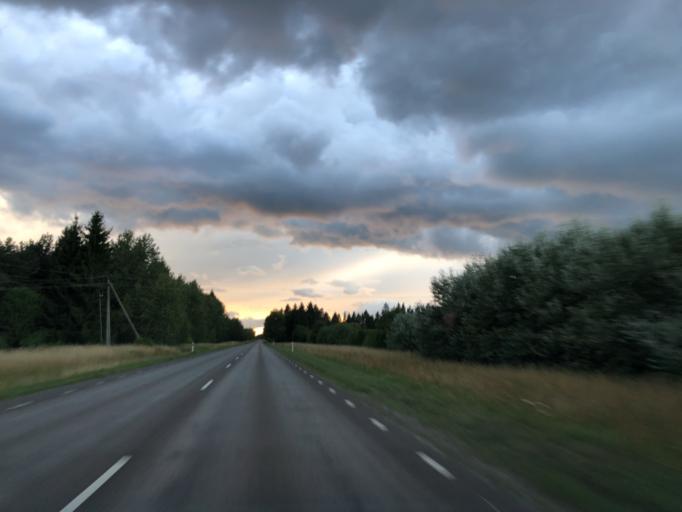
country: EE
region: Laeaene
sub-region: Ridala Parish
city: Uuemoisa
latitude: 58.8718
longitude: 23.6166
